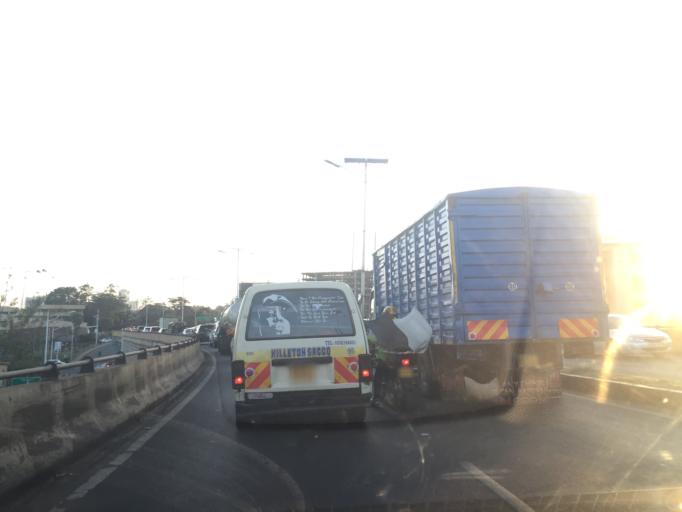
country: KE
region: Nairobi Area
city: Nairobi
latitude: -1.2709
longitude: 36.8149
